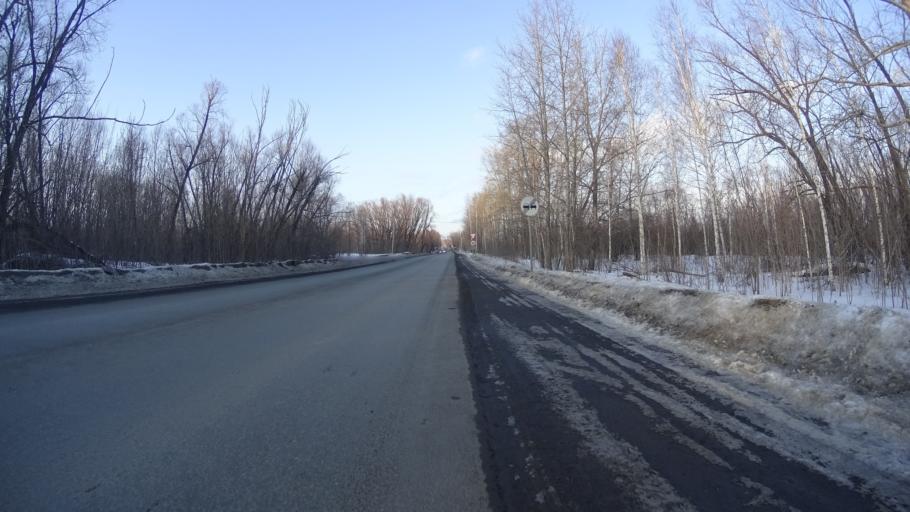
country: RU
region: Chelyabinsk
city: Sargazy
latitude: 55.1411
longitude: 61.2822
